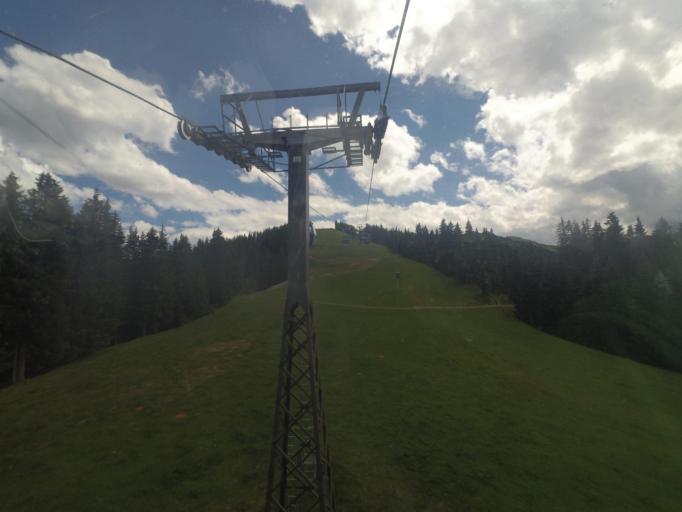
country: AT
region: Salzburg
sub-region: Politischer Bezirk Zell am See
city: Leogang
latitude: 47.4194
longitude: 12.7142
